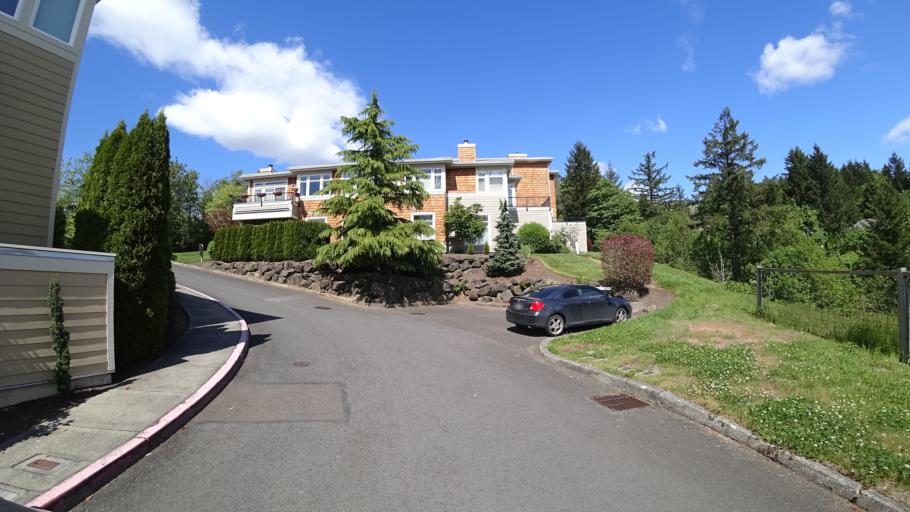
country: US
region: Oregon
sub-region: Washington County
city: West Haven
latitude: 45.5447
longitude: -122.7746
